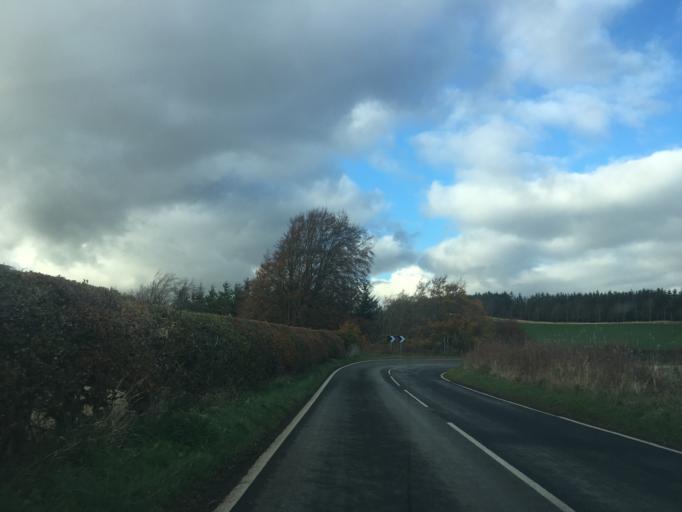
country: GB
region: Scotland
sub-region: East Lothian
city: Pencaitland
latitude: 55.8481
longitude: -2.8757
